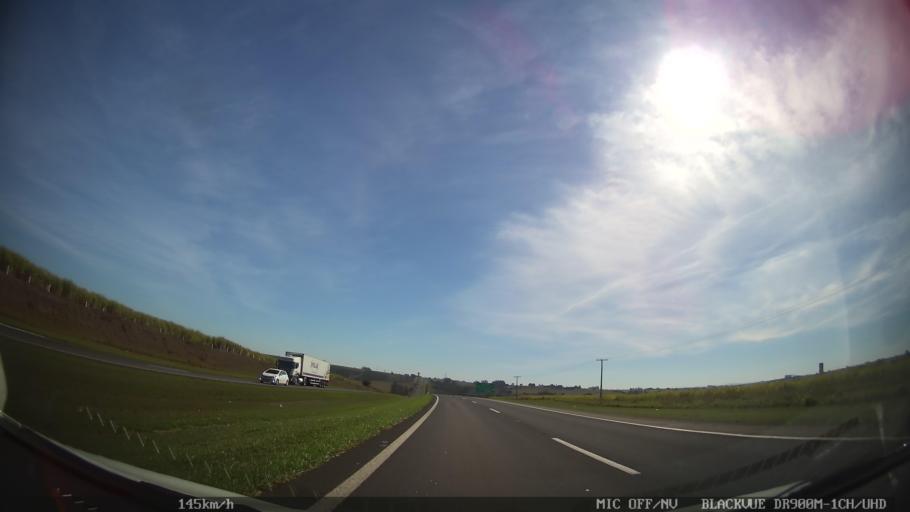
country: BR
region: Sao Paulo
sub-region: Leme
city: Leme
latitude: -22.1079
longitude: -47.4126
